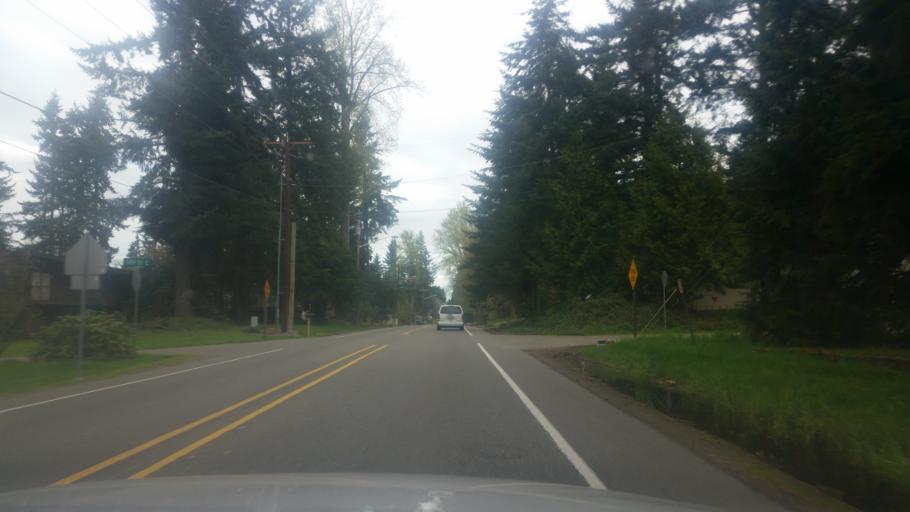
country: US
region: Washington
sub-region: Pierce County
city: South Hill
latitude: 47.1207
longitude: -122.2667
